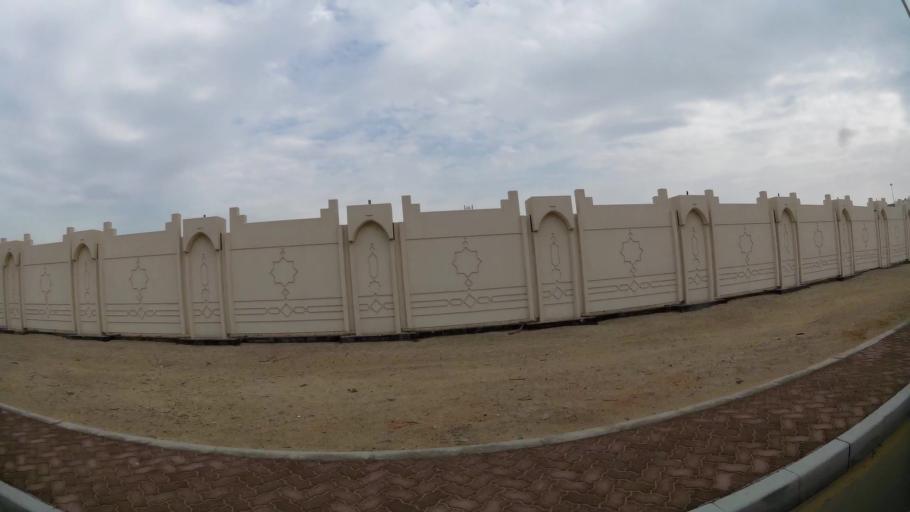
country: AE
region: Abu Dhabi
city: Abu Dhabi
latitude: 24.4258
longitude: 54.4135
